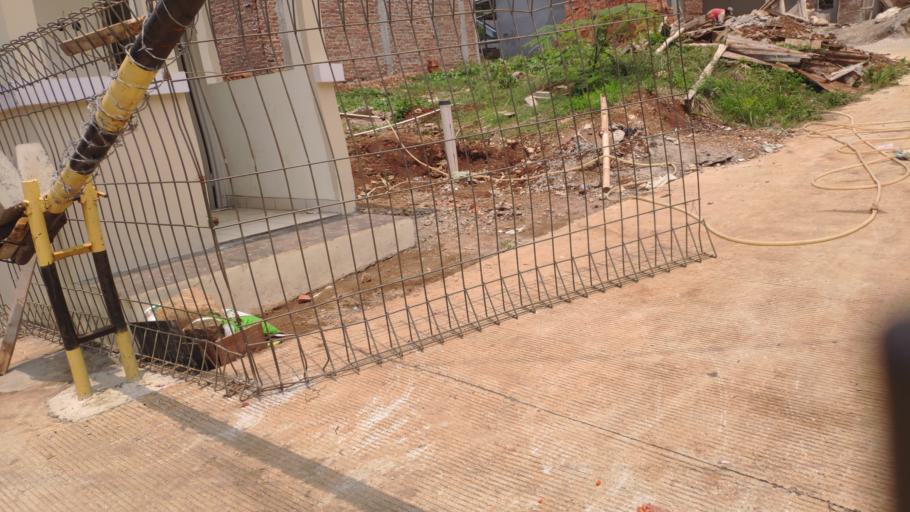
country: ID
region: West Java
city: Sawangan
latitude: -6.3910
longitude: 106.7935
